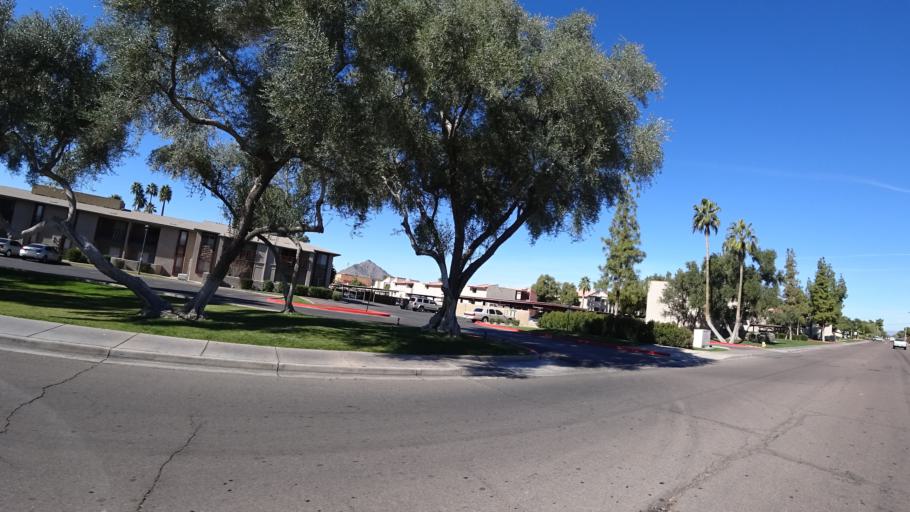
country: US
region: Arizona
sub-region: Maricopa County
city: Scottsdale
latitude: 33.5000
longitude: -111.9046
